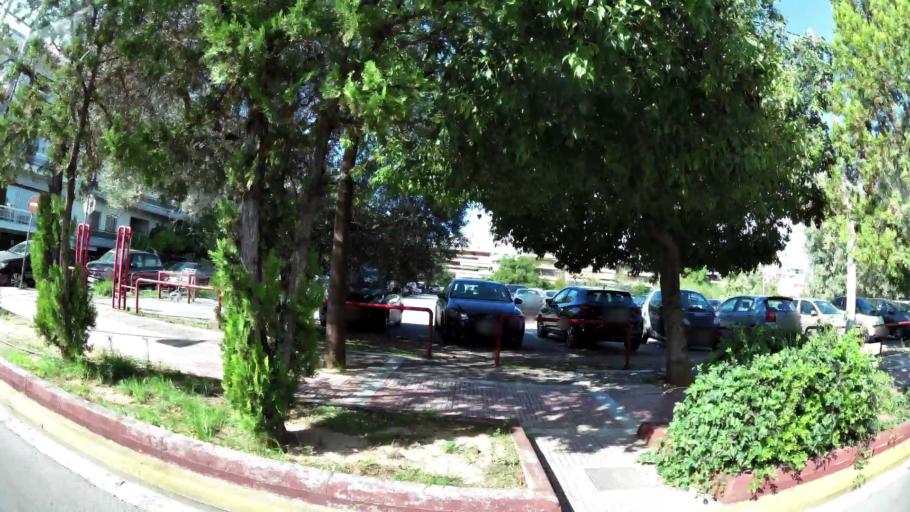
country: GR
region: Attica
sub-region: Nomarchia Athinas
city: Neo Psychiko
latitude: 38.0074
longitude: 23.7869
